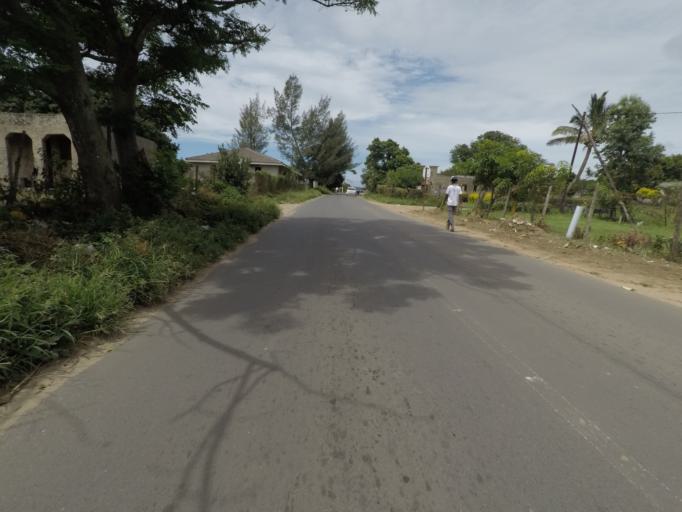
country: ZA
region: KwaZulu-Natal
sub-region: uThungulu District Municipality
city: eSikhawini
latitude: -28.8829
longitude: 31.9065
